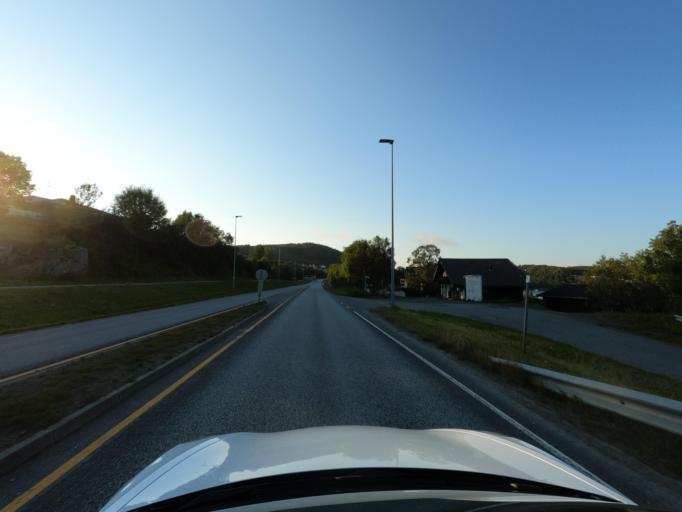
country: NO
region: Troms
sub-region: Harstad
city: Harstad
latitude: 68.7671
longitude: 16.5593
